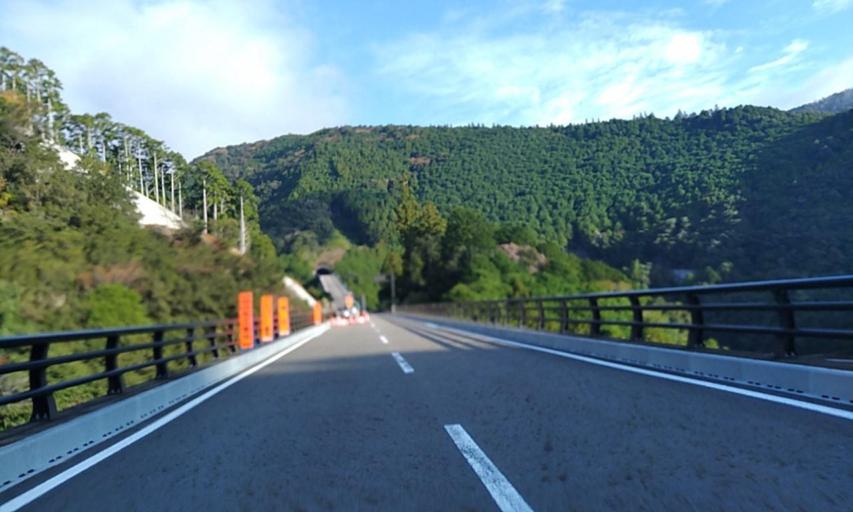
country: JP
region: Wakayama
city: Shingu
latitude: 33.8913
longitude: 135.8798
